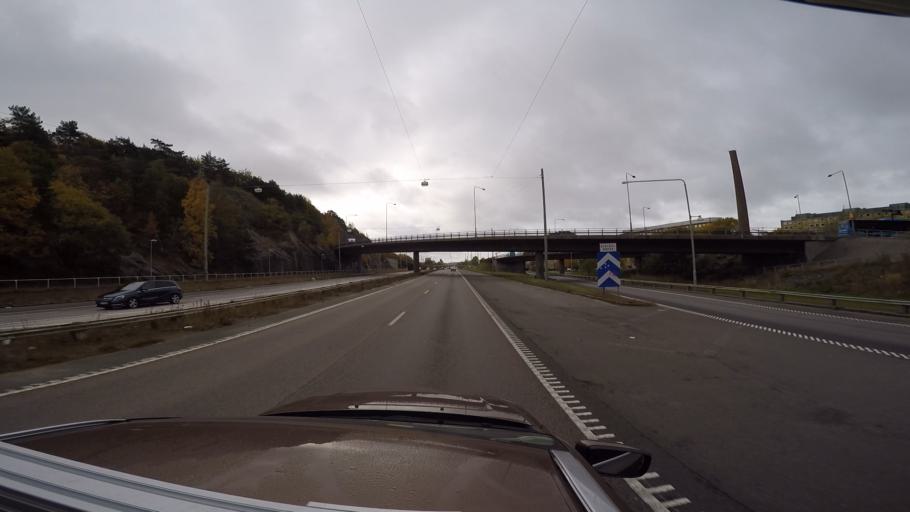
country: SE
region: Vaestra Goetaland
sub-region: Goteborg
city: Majorna
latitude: 57.6729
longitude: 11.9390
